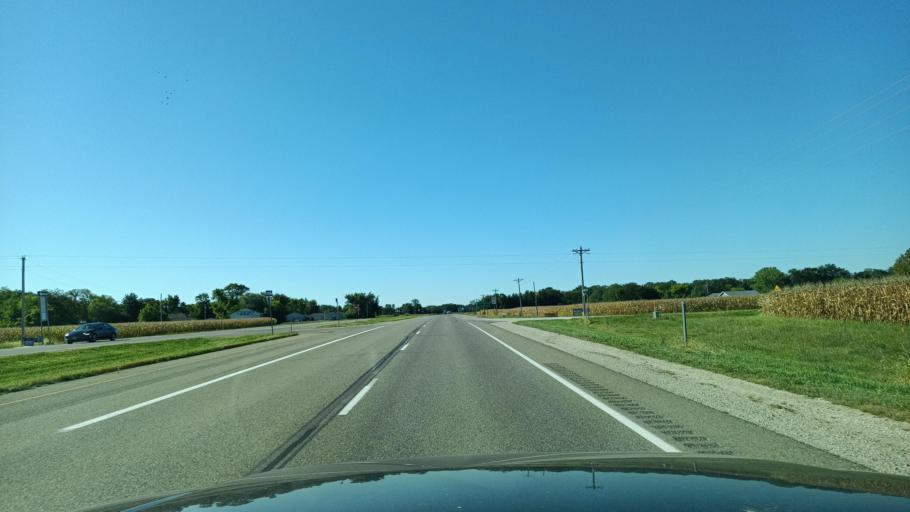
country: US
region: Iowa
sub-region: Lee County
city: Fort Madison
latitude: 40.6876
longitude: -91.2502
